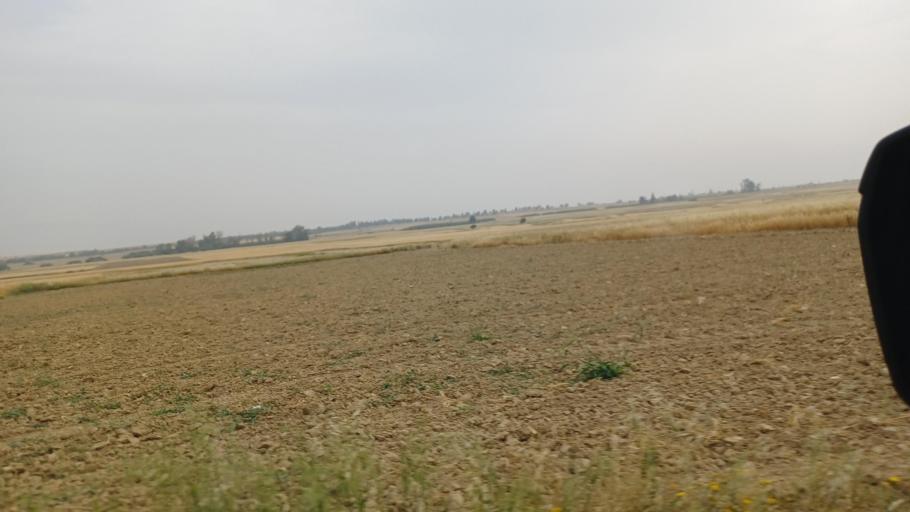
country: CY
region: Lefkosia
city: Mammari
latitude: 35.1727
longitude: 33.2244
